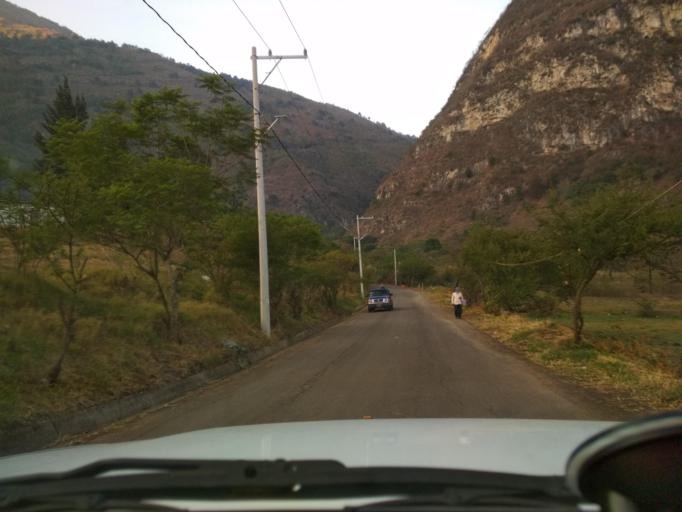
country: MX
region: Veracruz
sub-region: Nogales
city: Taza de Agua Ojo Zarco
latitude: 18.7748
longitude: -97.1954
